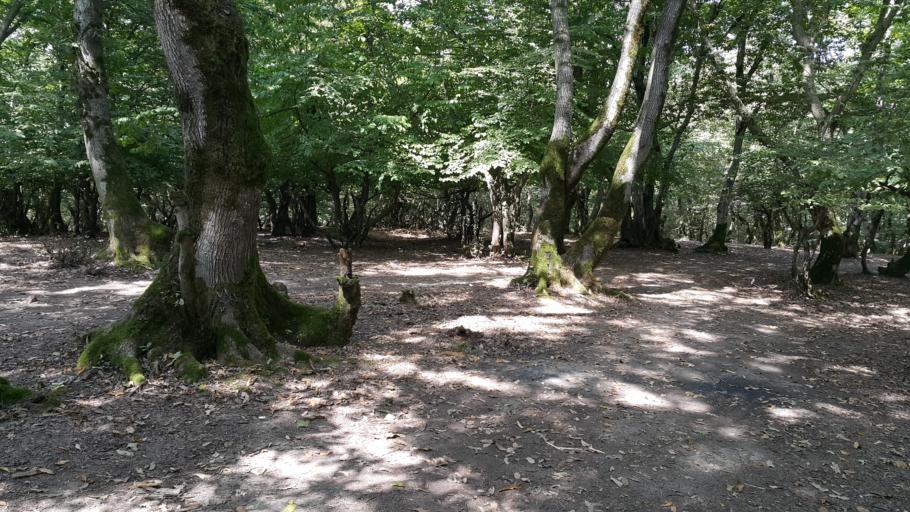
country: IR
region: Gilan
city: Shaft
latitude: 37.1526
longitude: 49.5246
